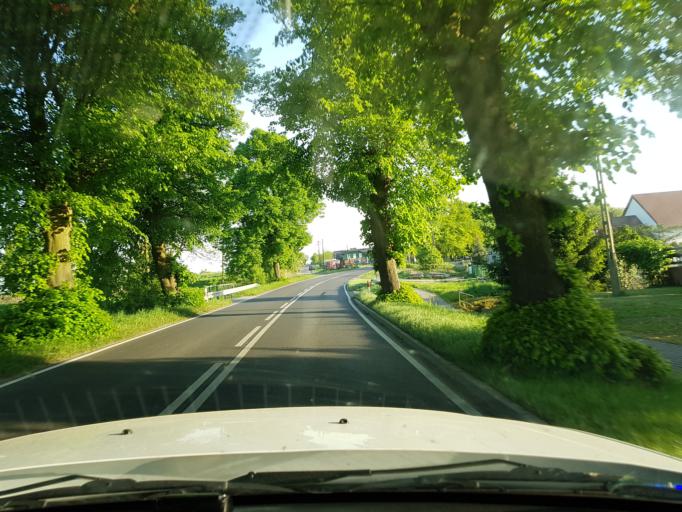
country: PL
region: West Pomeranian Voivodeship
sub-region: Powiat goleniowski
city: Maszewo
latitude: 53.4888
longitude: 15.0640
